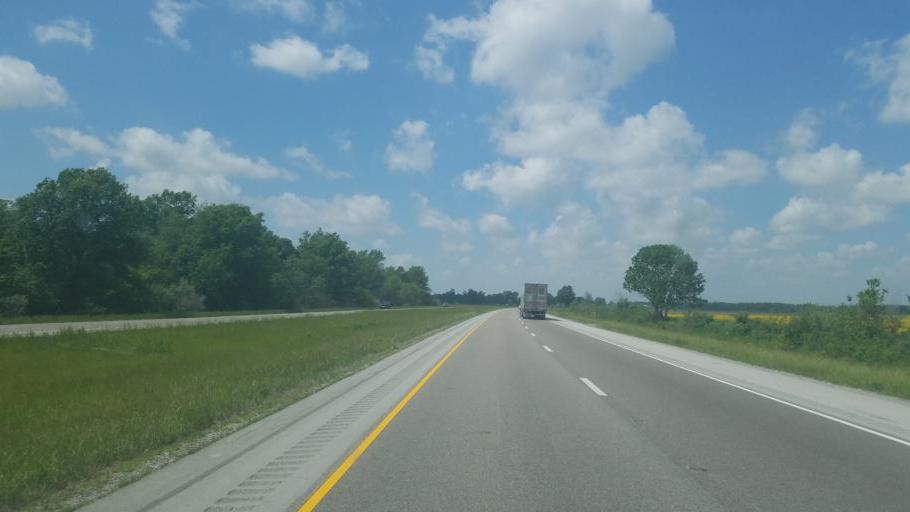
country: US
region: Illinois
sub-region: Cumberland County
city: Greenup
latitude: 39.2386
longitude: -88.1988
